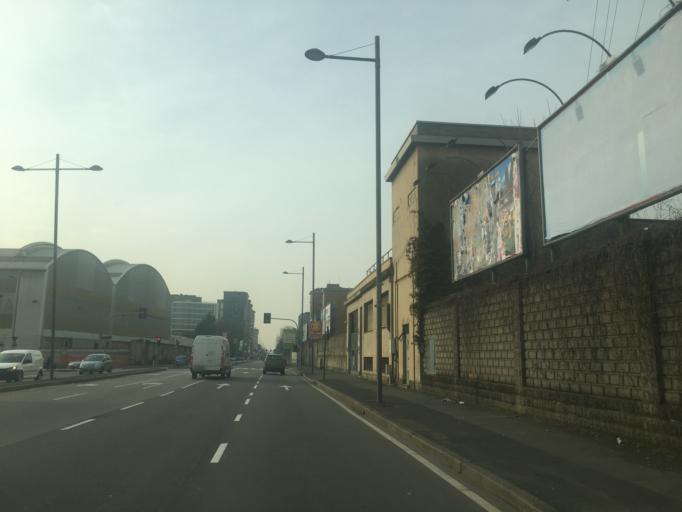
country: IT
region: Lombardy
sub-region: Citta metropolitana di Milano
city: Sesto San Giovanni
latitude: 45.5292
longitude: 9.2163
